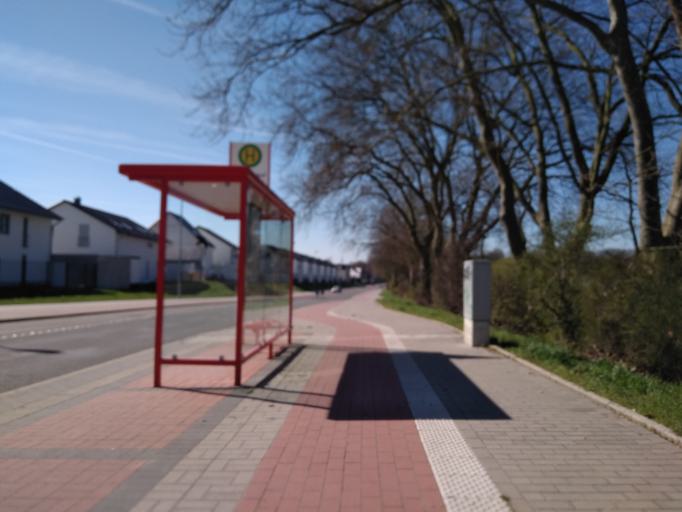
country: DE
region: North Rhine-Westphalia
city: Marl
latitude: 51.6026
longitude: 7.0670
